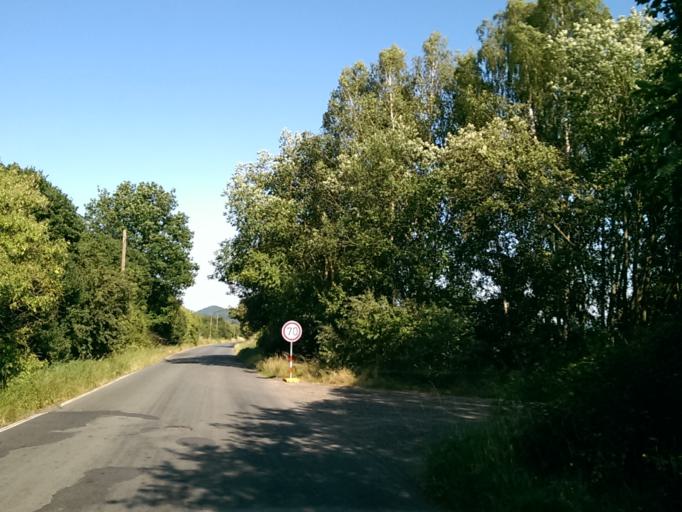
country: CZ
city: Duba
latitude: 50.5426
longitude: 14.5234
